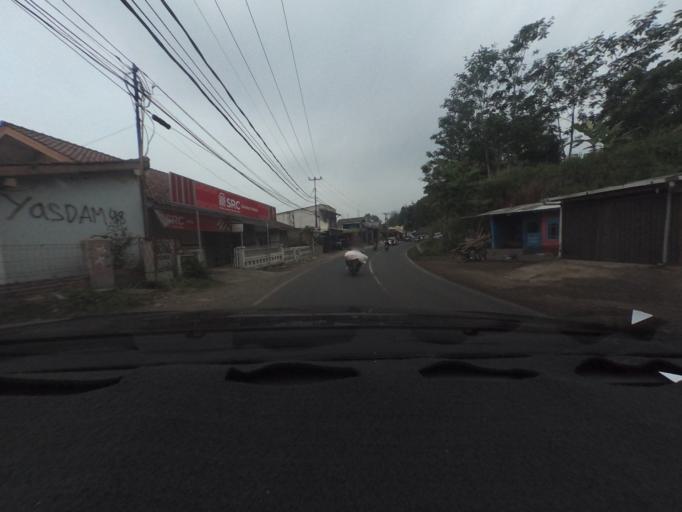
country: ID
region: West Java
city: Cicurug
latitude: -6.8044
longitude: 106.7723
